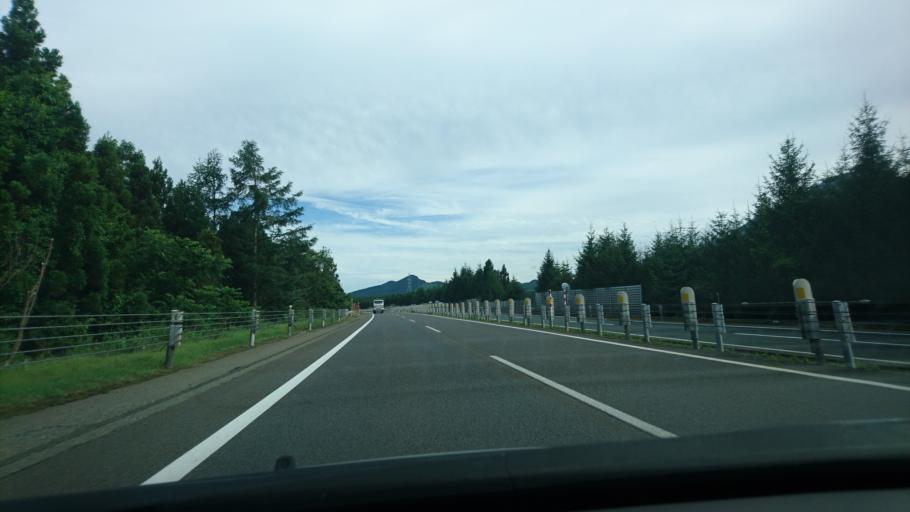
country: JP
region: Iwate
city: Shizukuishi
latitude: 39.9244
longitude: 141.0346
